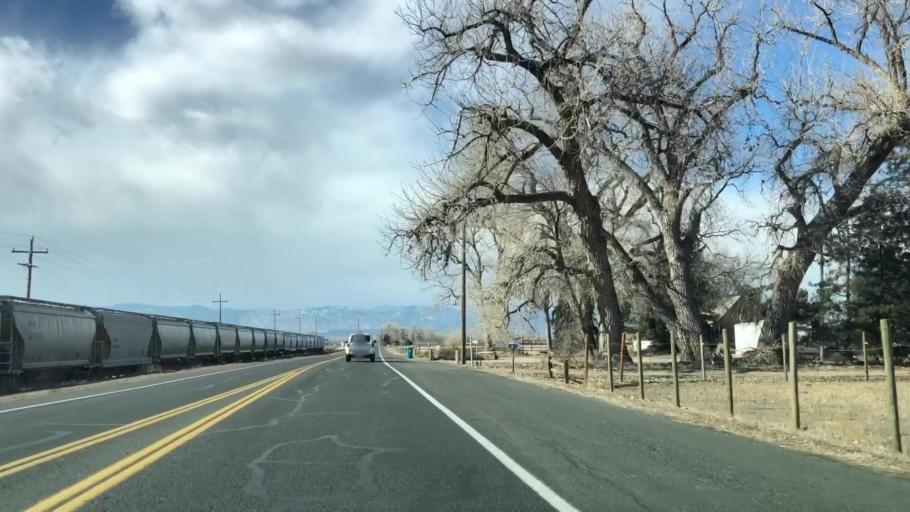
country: US
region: Colorado
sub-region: Larimer County
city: Fort Collins
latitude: 40.5960
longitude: -105.0205
